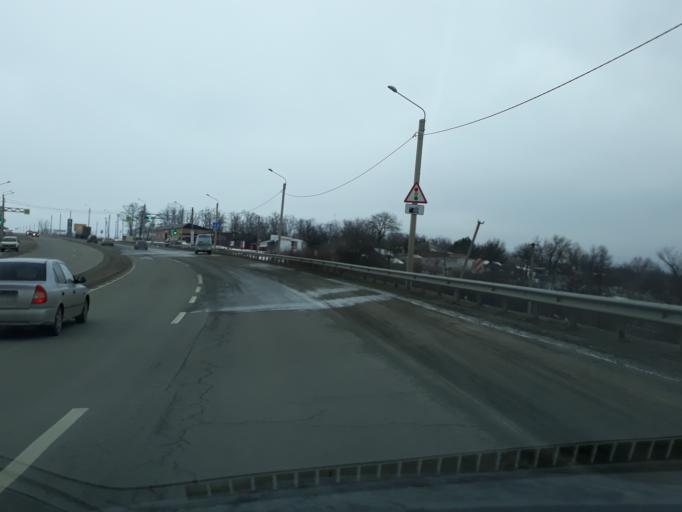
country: RU
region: Rostov
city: Sinyavskoye
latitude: 47.2988
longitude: 39.2146
